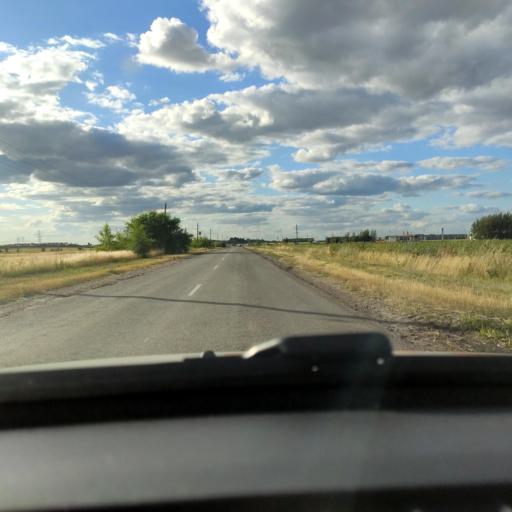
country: RU
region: Voronezj
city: Orlovo
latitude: 51.6742
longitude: 39.6847
